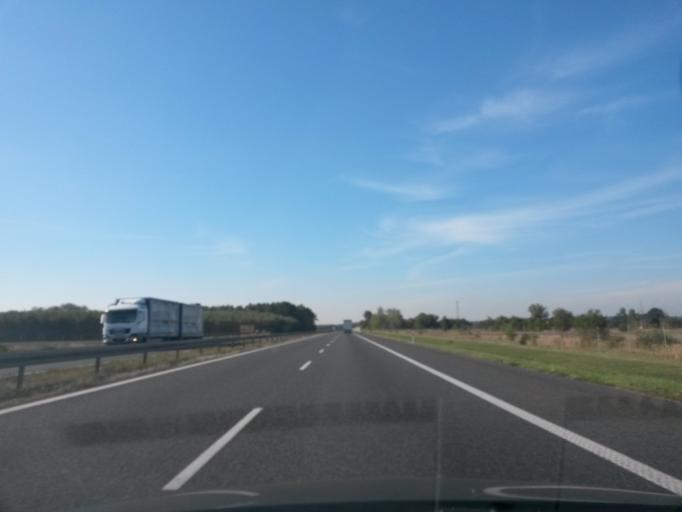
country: PL
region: Silesian Voivodeship
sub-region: Powiat gliwicki
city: Rudziniec
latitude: 50.3743
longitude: 18.4829
